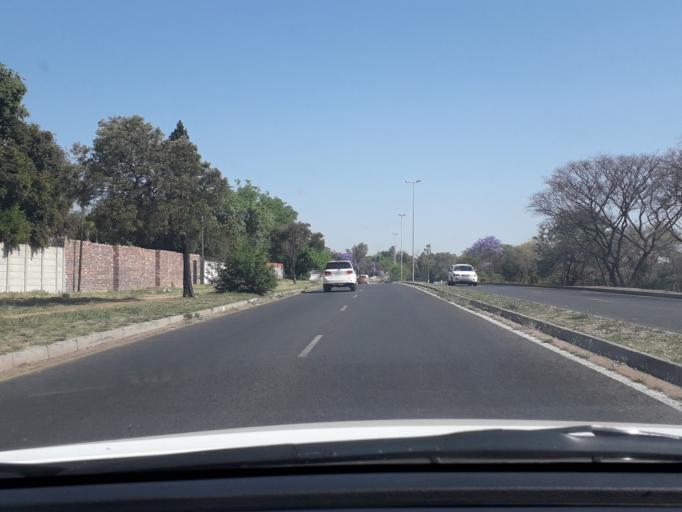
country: ZA
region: Gauteng
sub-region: City of Johannesburg Metropolitan Municipality
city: Roodepoort
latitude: -26.0938
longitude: 27.9616
